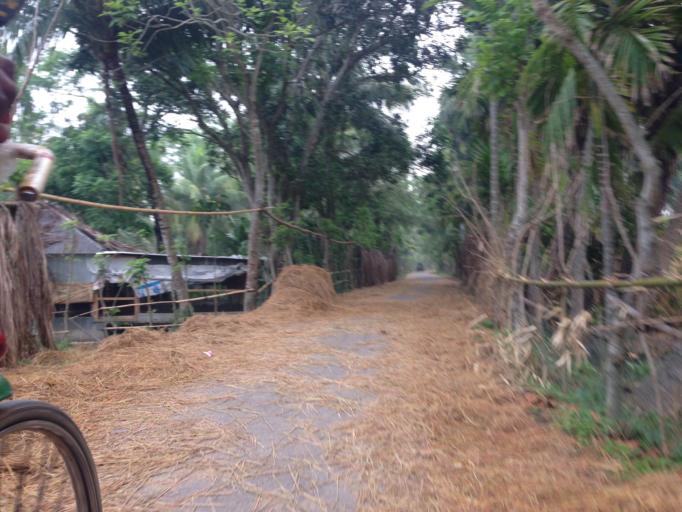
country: BD
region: Khulna
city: Kalia
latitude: 23.0418
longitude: 89.6449
